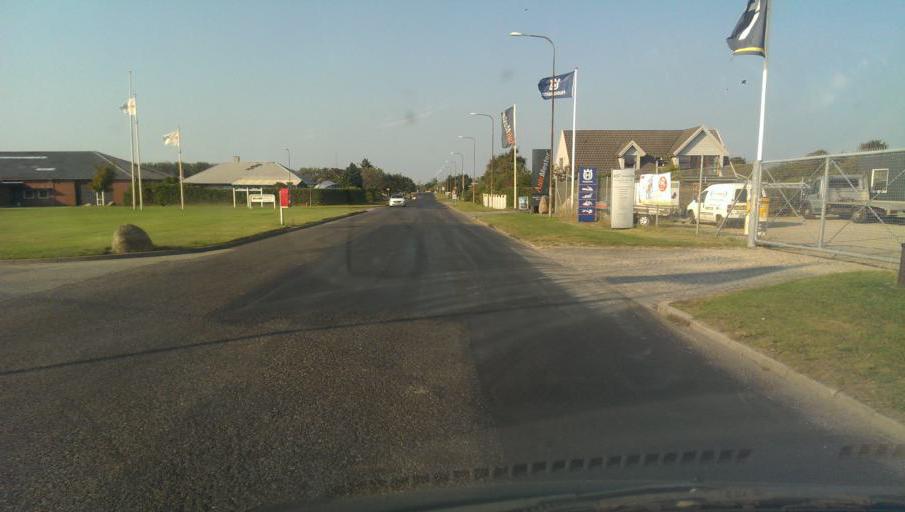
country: DK
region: South Denmark
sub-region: Esbjerg Kommune
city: Esbjerg
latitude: 55.5061
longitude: 8.4174
